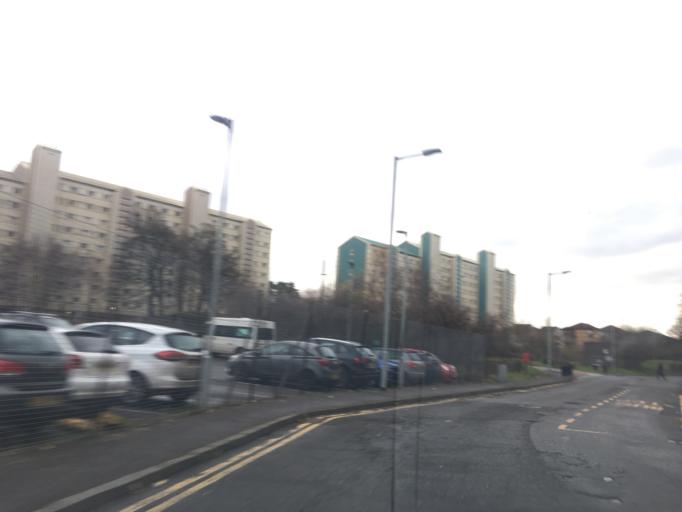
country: GB
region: Scotland
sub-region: Edinburgh
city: Colinton
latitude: 55.9185
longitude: -3.2732
